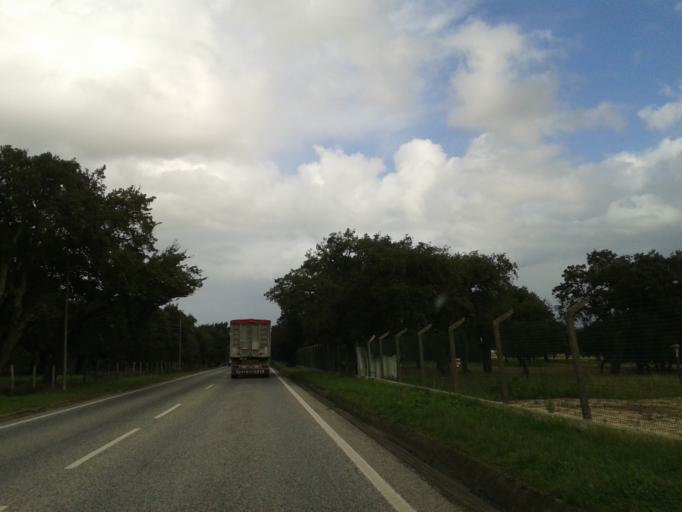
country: PT
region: Setubal
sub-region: Alcochete
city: Alcochete
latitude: 38.7617
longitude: -8.9083
